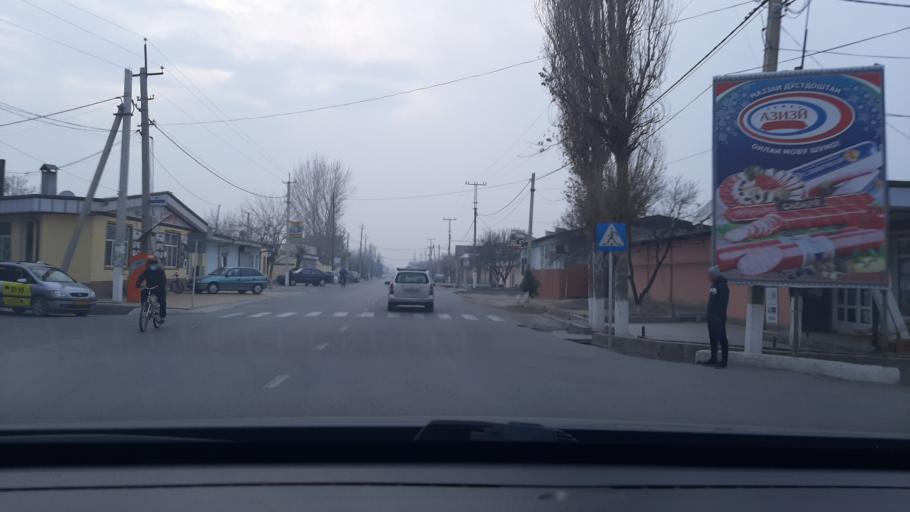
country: TJ
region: Viloyati Sughd
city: Khujand
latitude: 40.2651
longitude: 69.6073
